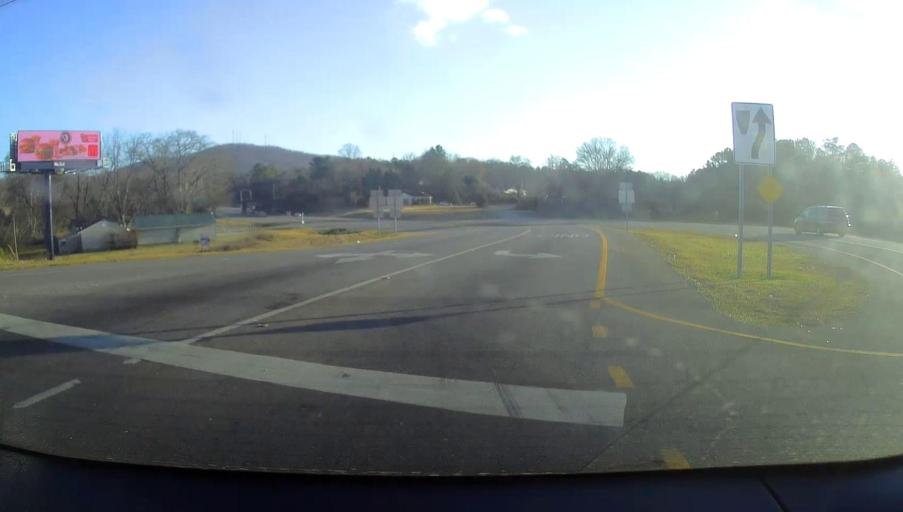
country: US
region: Alabama
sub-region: Calhoun County
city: Saks
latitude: 33.7004
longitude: -85.8279
